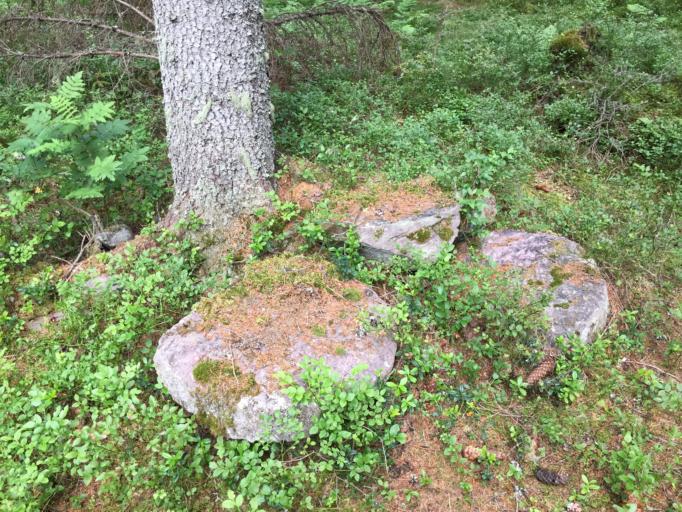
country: SE
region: Dalarna
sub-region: Malung-Saelens kommun
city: Malung
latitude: 60.6391
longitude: 13.7760
